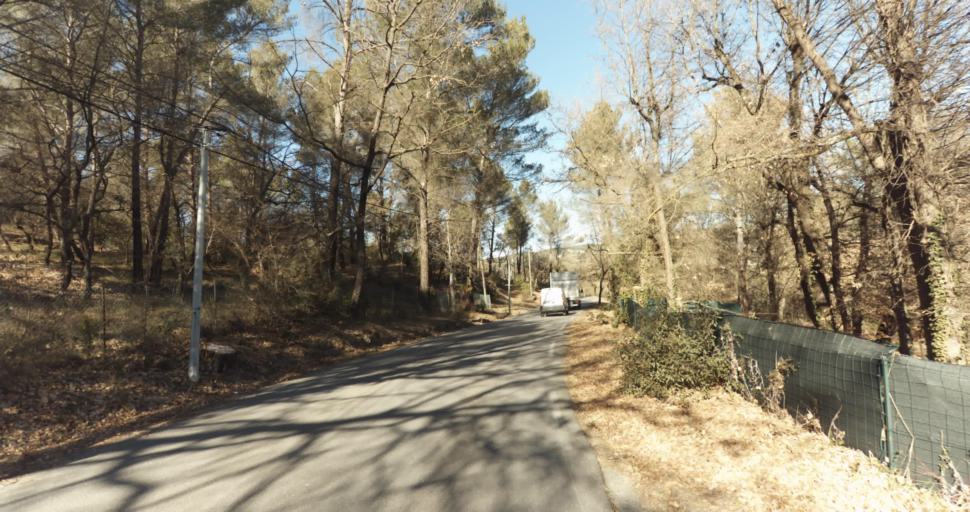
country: FR
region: Provence-Alpes-Cote d'Azur
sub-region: Departement des Bouches-du-Rhone
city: Peypin
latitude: 43.3917
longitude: 5.5718
